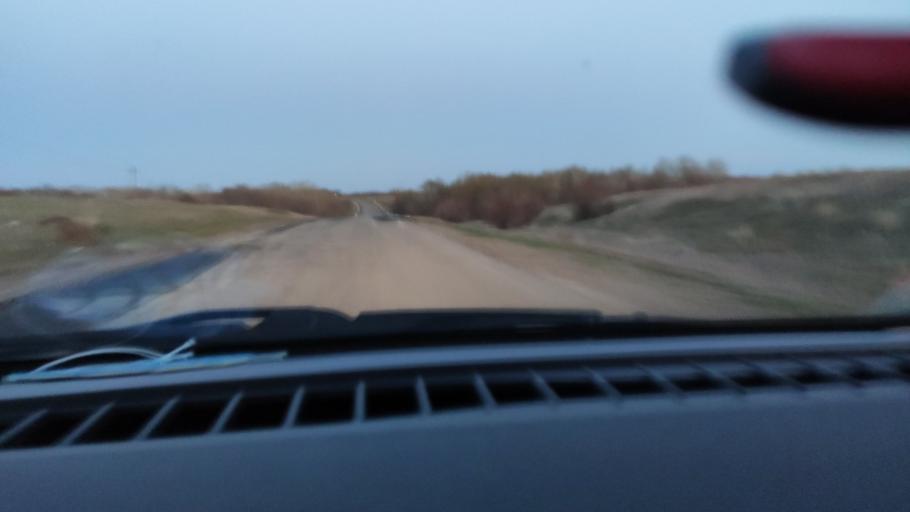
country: RU
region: Saratov
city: Rovnoye
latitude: 51.0460
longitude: 46.0530
